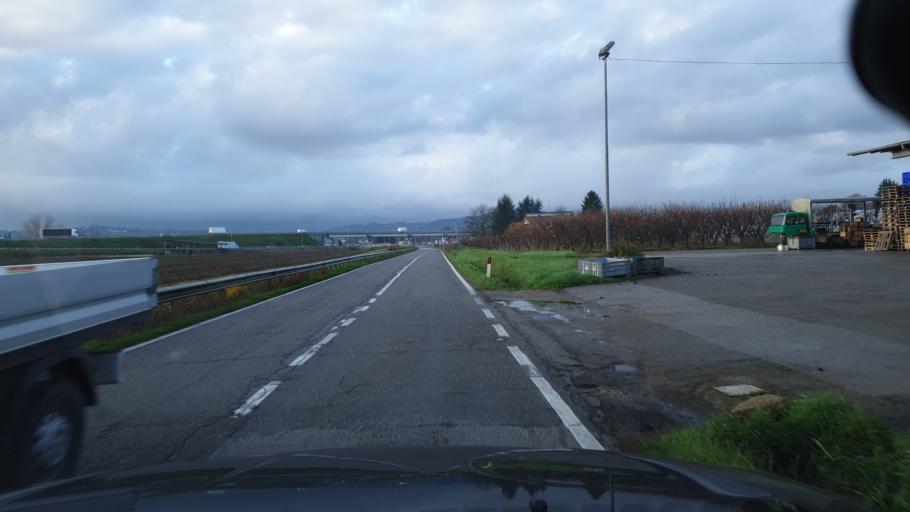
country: IT
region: Emilia-Romagna
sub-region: Provincia di Bologna
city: Crespellano
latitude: 44.5197
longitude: 11.1158
